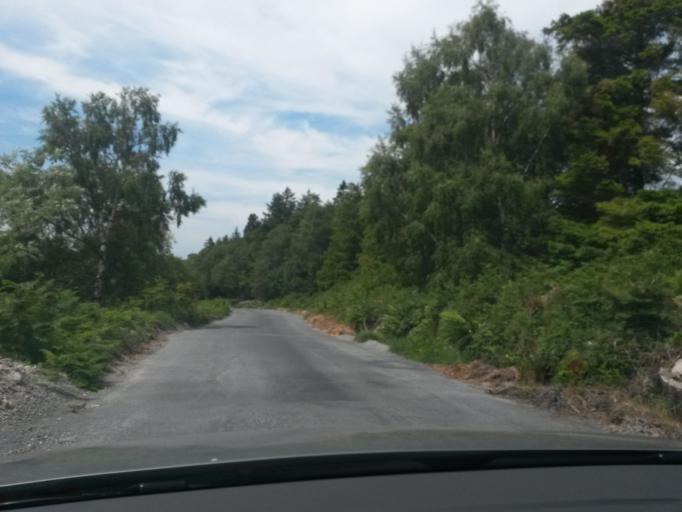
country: IE
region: Leinster
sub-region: Wicklow
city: Enniskerry
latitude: 53.1900
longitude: -6.2412
